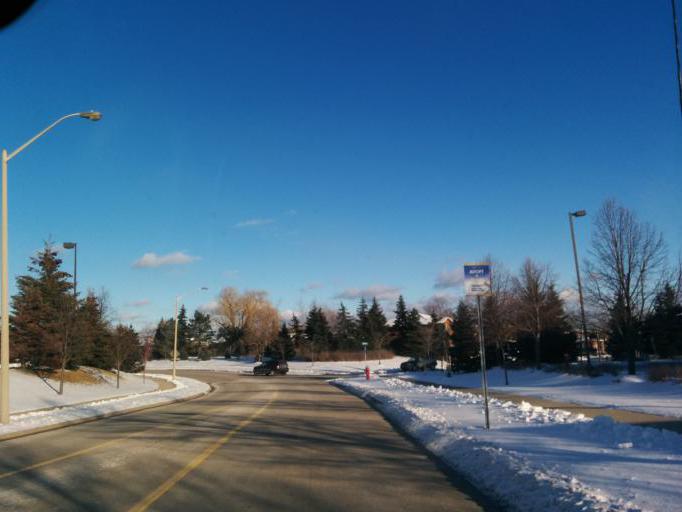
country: CA
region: Ontario
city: Oakville
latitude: 43.5029
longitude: -79.6693
